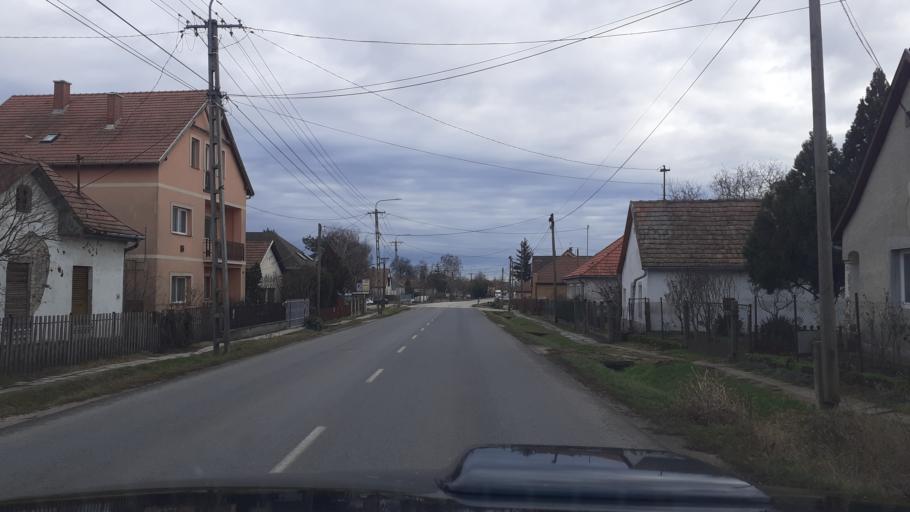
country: HU
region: Fejer
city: Seregelyes
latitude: 47.1170
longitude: 18.5703
